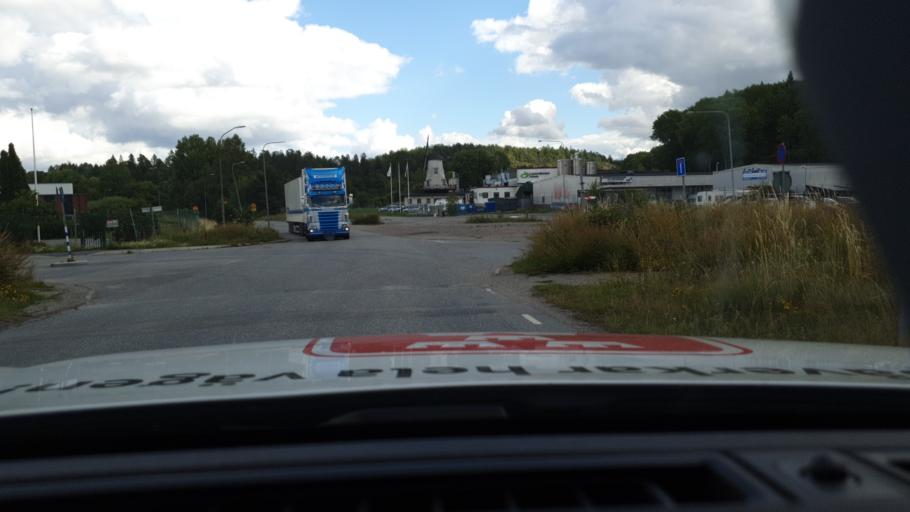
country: SE
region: Stockholm
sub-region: Huddinge Kommun
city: Huddinge
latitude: 59.2219
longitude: 17.9610
